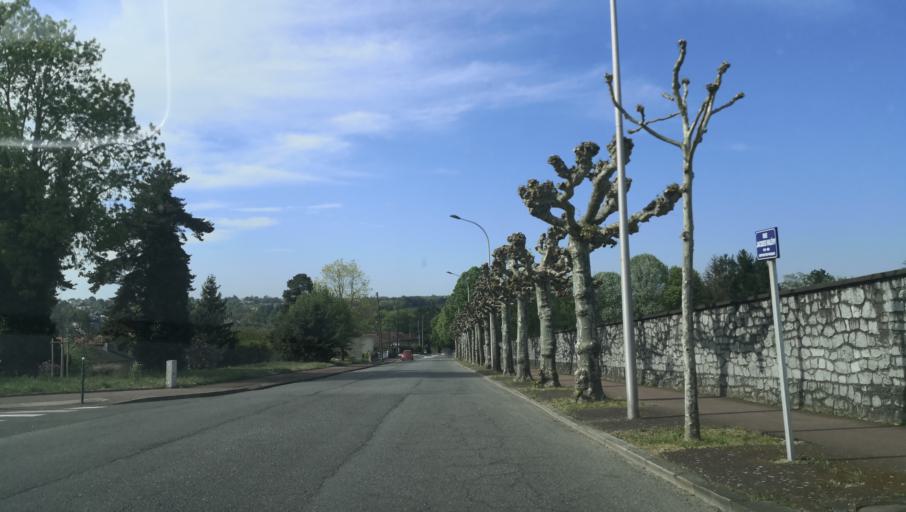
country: FR
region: Limousin
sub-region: Departement de la Haute-Vienne
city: Couzeix
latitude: 45.8569
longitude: 1.2588
